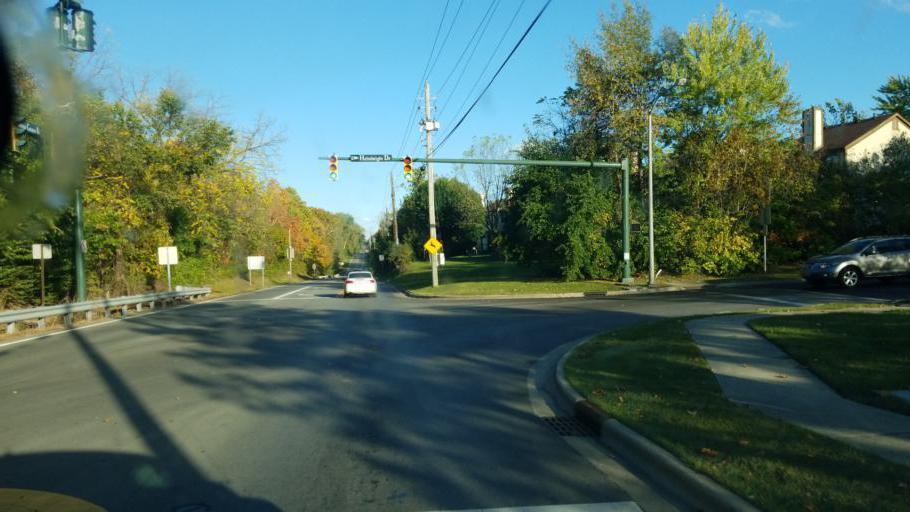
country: US
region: Ohio
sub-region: Franklin County
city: Gahanna
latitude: 40.0176
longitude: -82.8525
